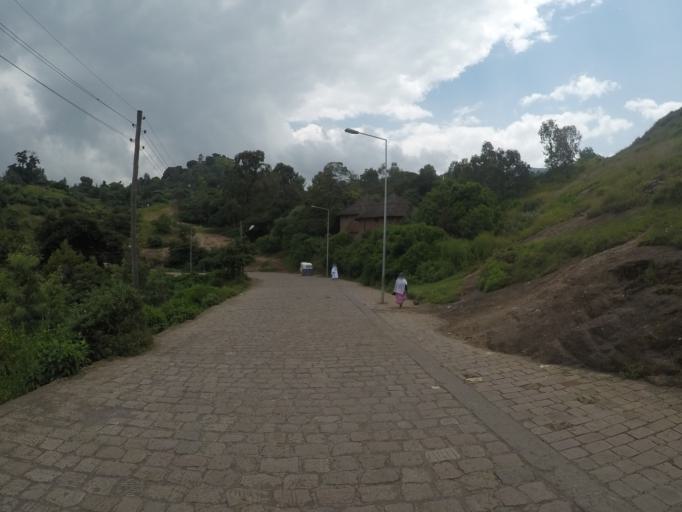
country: ET
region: Amhara
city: Lalibela
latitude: 12.0311
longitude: 39.0431
